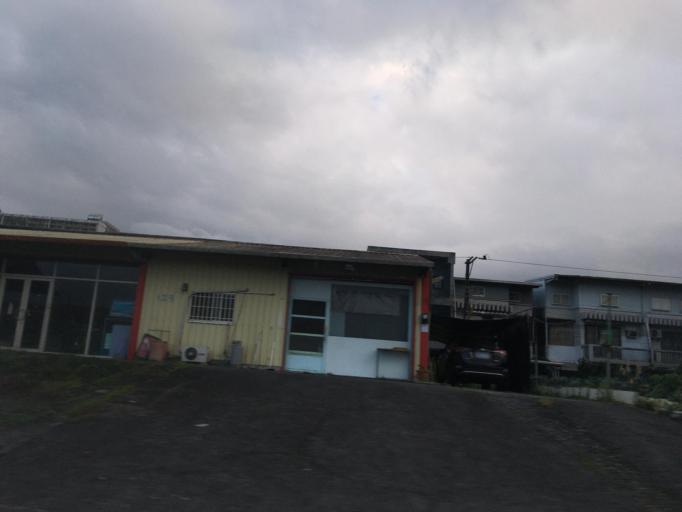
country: TW
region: Taiwan
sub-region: Yilan
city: Yilan
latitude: 24.7570
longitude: 121.7440
